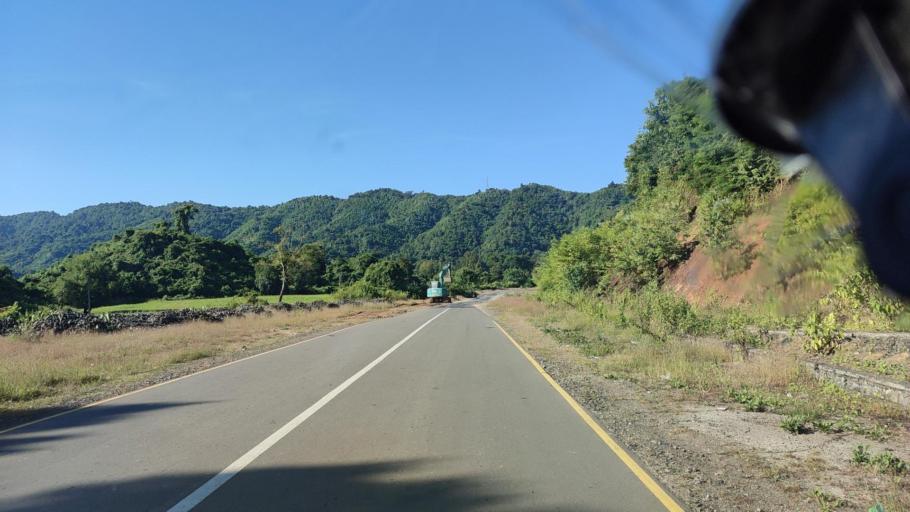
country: MM
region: Rakhine
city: Sittwe
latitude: 19.9322
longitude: 93.7857
